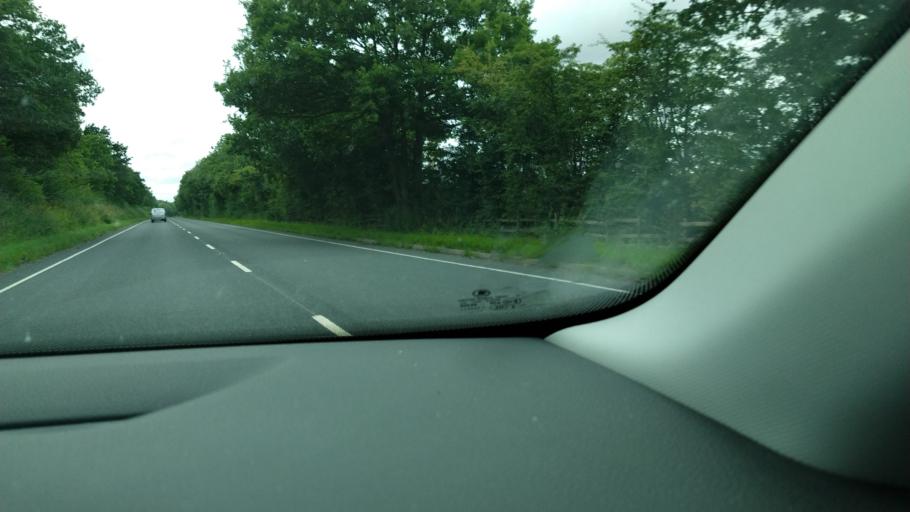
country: GB
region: England
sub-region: East Riding of Yorkshire
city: Barmby on the Marsh
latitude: 53.7212
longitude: -0.9774
